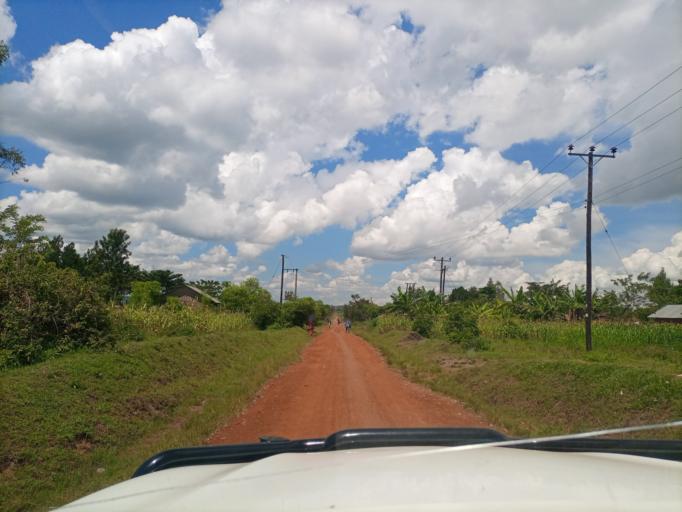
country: UG
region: Eastern Region
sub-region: Tororo District
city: Tororo
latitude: 0.6444
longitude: 33.9953
